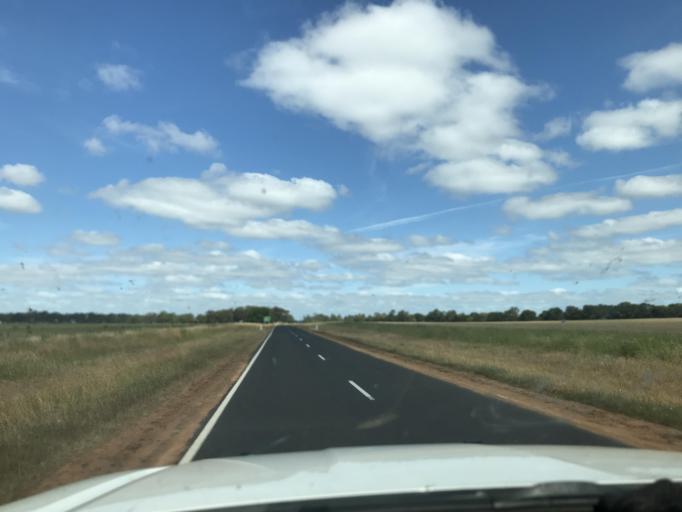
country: AU
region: South Australia
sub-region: Naracoorte and Lucindale
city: Naracoorte
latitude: -37.0168
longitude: 141.2996
